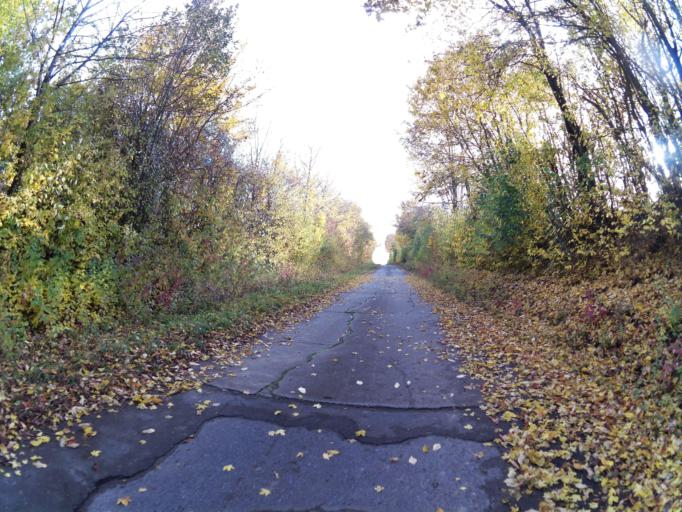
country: DE
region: Bavaria
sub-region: Regierungsbezirk Unterfranken
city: Giebelstadt
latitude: 49.6679
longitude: 9.9643
